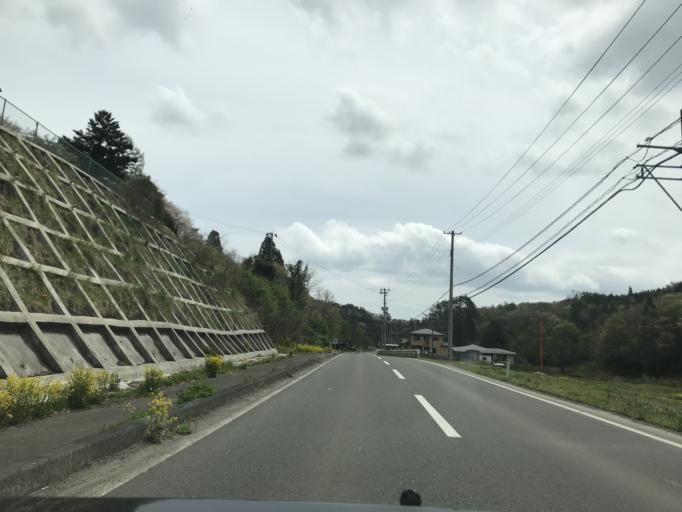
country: JP
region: Iwate
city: Ichinoseki
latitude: 38.8044
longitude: 141.3859
